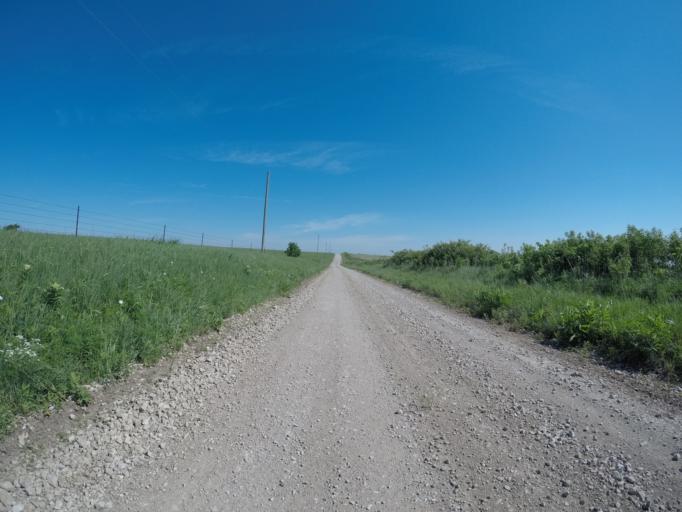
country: US
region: Kansas
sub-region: Wabaunsee County
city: Alma
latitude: 38.9532
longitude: -96.1138
